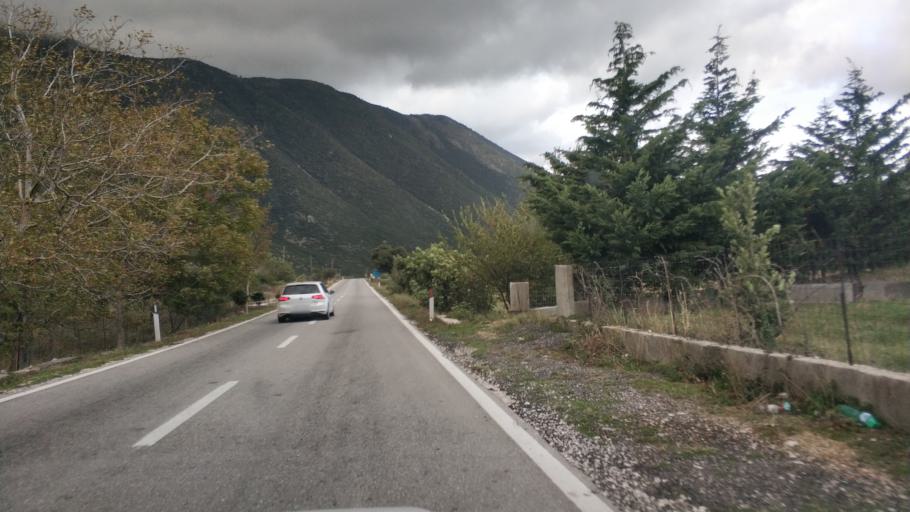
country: AL
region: Vlore
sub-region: Rrethi i Vlores
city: Brataj
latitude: 40.2309
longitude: 19.5692
